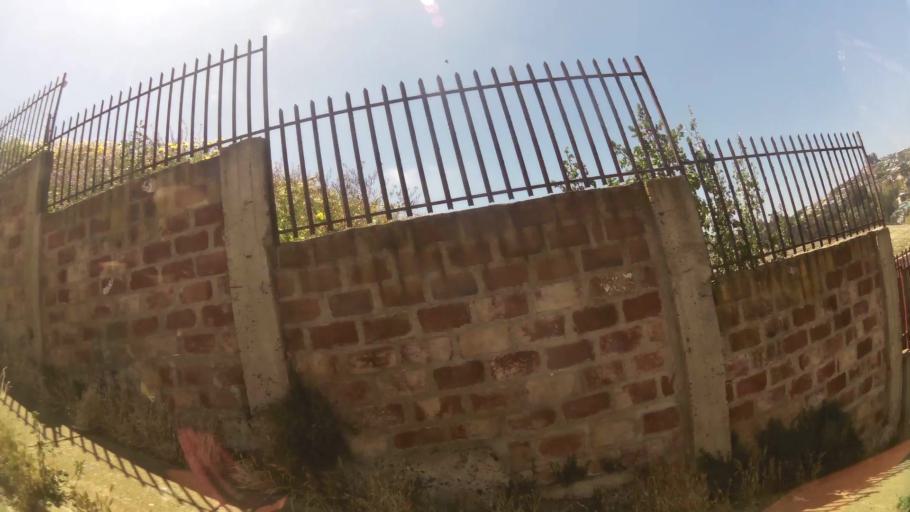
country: CL
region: Valparaiso
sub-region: Provincia de Valparaiso
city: Valparaiso
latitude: -33.0309
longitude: -71.6488
